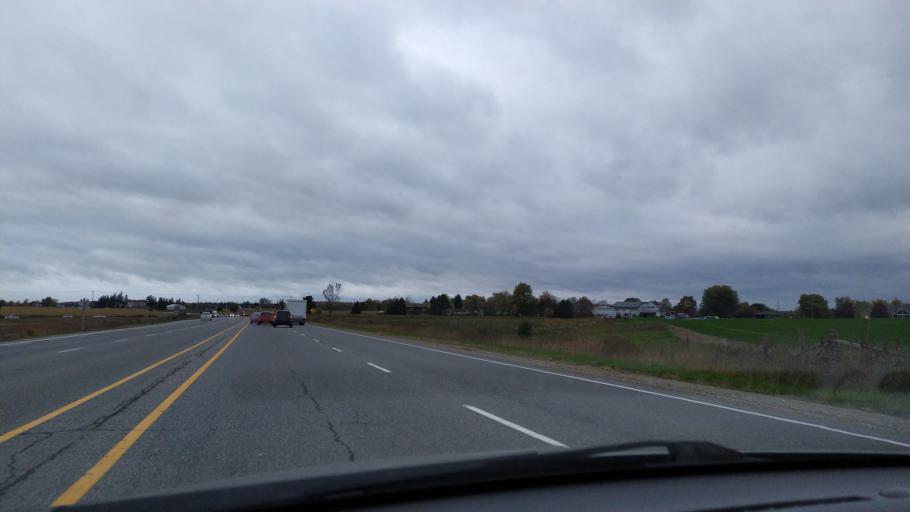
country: CA
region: Ontario
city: Stratford
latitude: 43.3665
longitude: -80.7312
